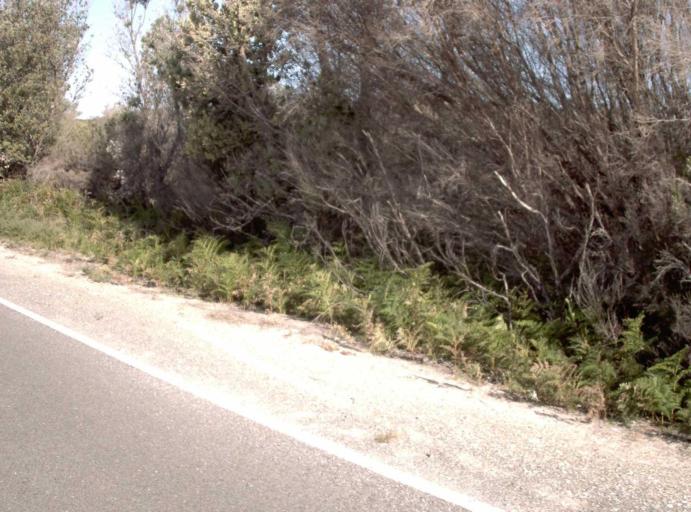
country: AU
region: Victoria
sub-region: East Gippsland
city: Lakes Entrance
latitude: -37.8019
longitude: 148.7277
